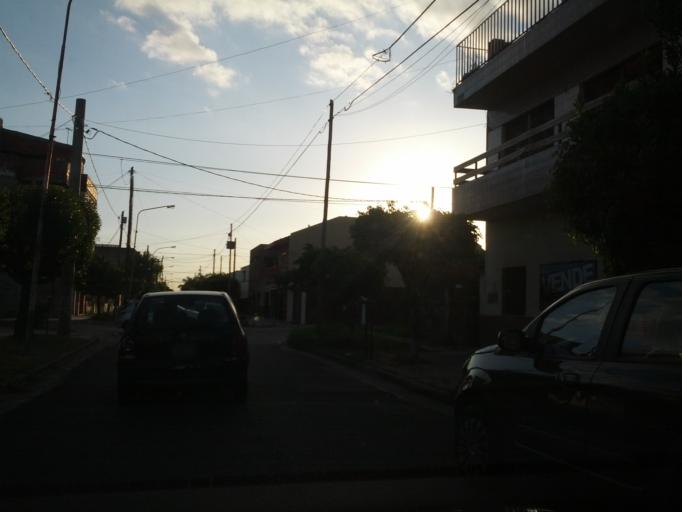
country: AR
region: Buenos Aires
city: San Justo
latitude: -34.6528
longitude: -58.5385
